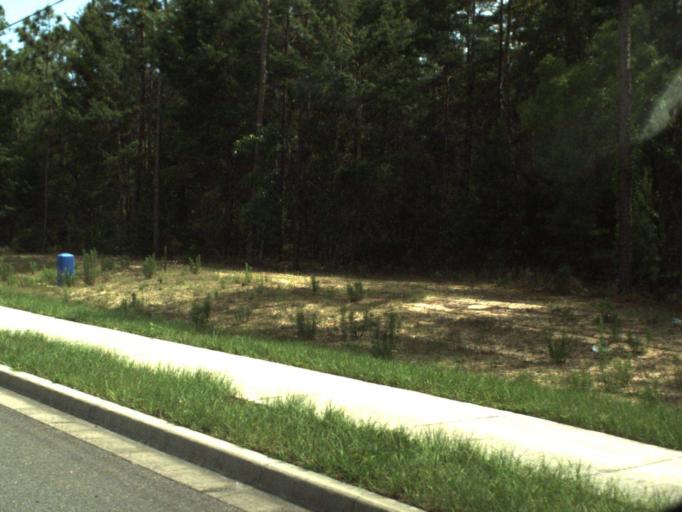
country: US
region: Florida
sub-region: Marion County
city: Ocala
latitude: 29.2094
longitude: -82.0574
